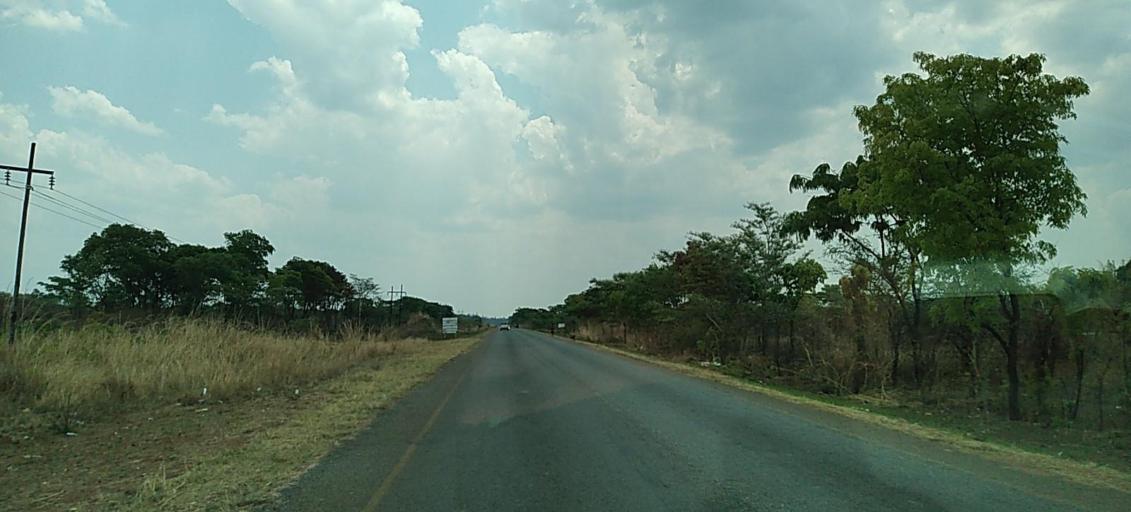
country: ZM
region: Copperbelt
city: Kalulushi
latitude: -12.8361
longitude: 27.9476
